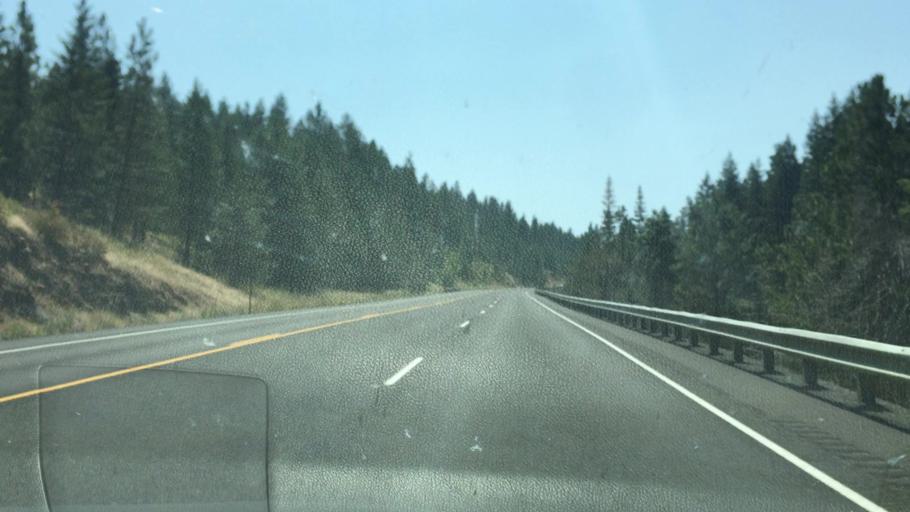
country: US
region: Idaho
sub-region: Idaho County
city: Grangeville
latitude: 45.8587
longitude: -116.2372
